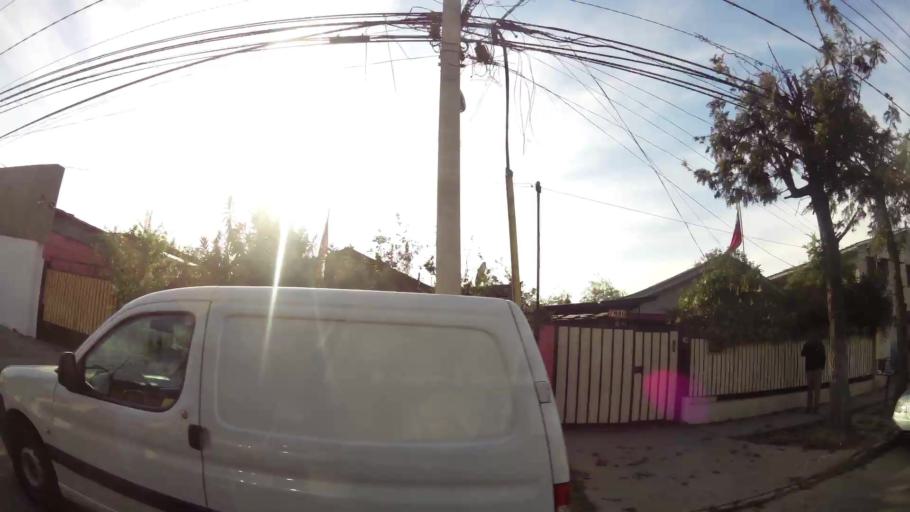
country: CL
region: Santiago Metropolitan
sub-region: Provincia de Santiago
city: La Pintana
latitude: -33.5255
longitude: -70.6628
